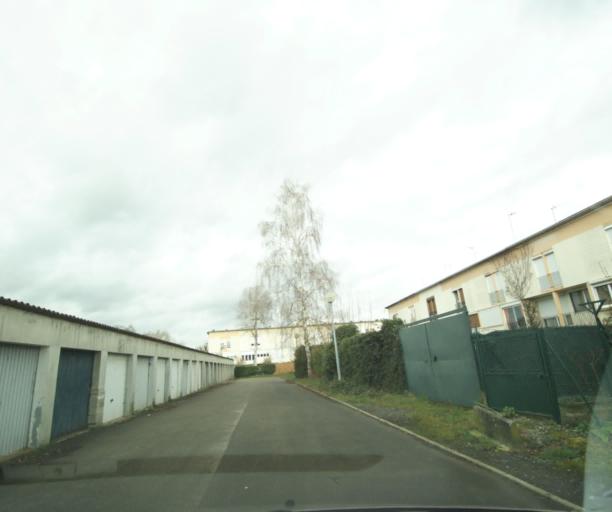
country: FR
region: Picardie
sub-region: Departement de l'Oise
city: Noyon
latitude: 49.5801
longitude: 2.9874
